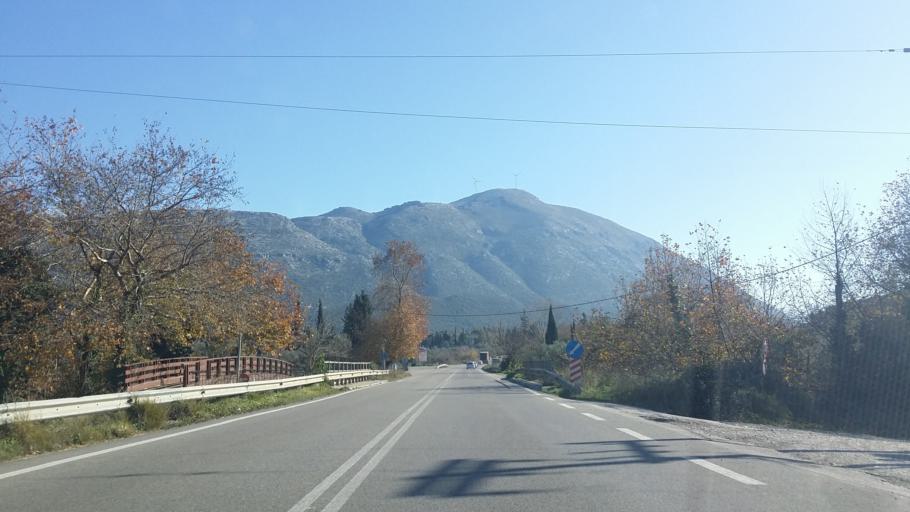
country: GR
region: West Greece
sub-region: Nomos Aitolias kai Akarnanias
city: Galatas
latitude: 38.3753
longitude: 21.6315
